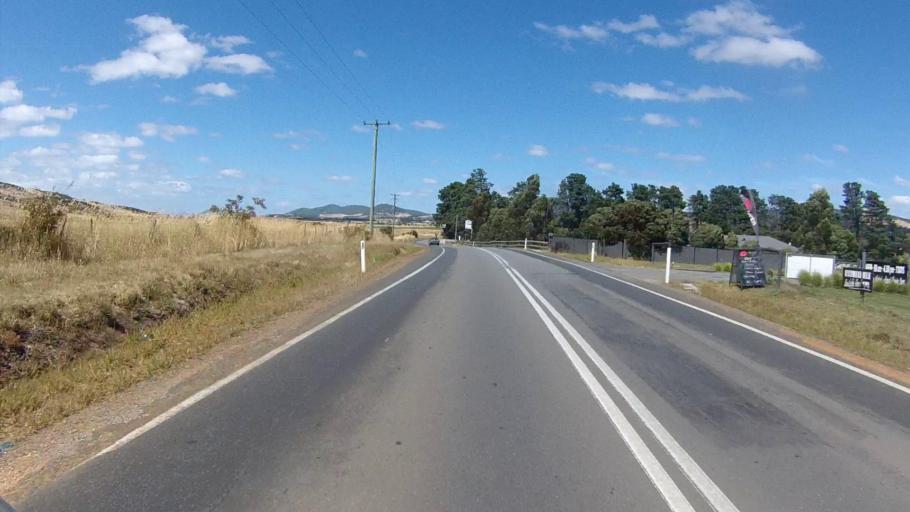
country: AU
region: Tasmania
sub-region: Clarence
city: Cambridge
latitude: -42.7520
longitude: 147.4164
